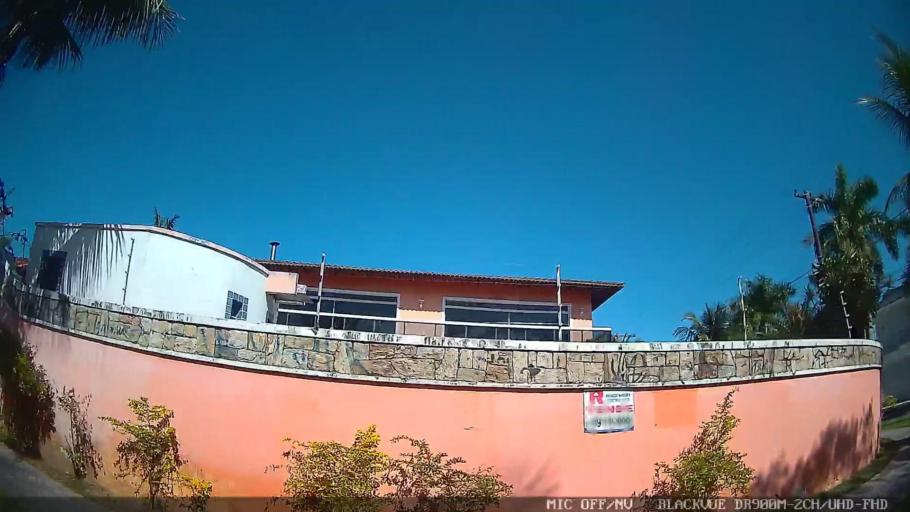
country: BR
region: Sao Paulo
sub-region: Guaruja
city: Guaruja
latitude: -23.9837
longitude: -46.2114
